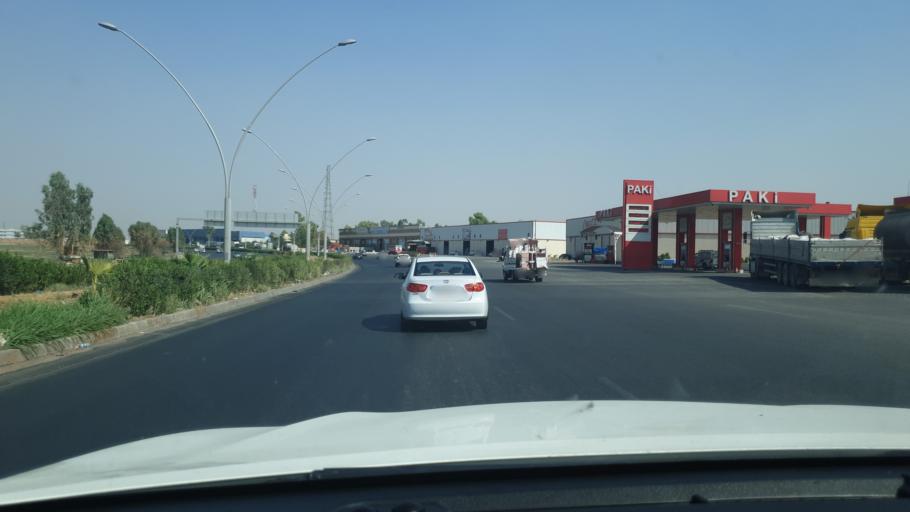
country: IQ
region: Arbil
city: Erbil
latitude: 36.1755
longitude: 43.9278
